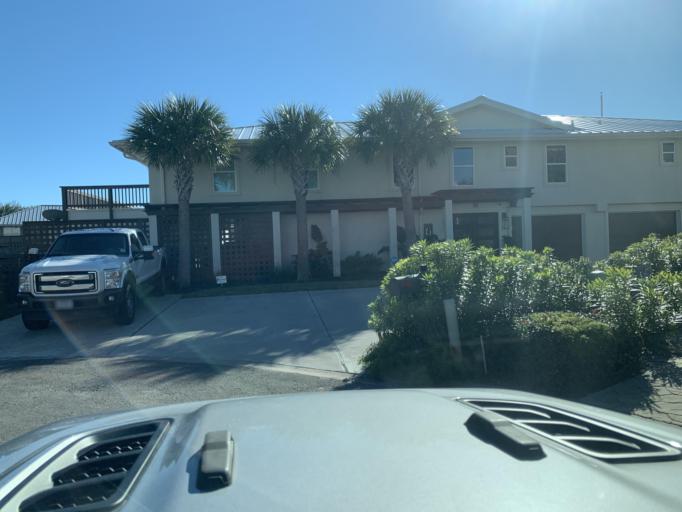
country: US
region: Texas
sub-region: Aransas County
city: Fulton
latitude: 28.0370
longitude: -97.0320
